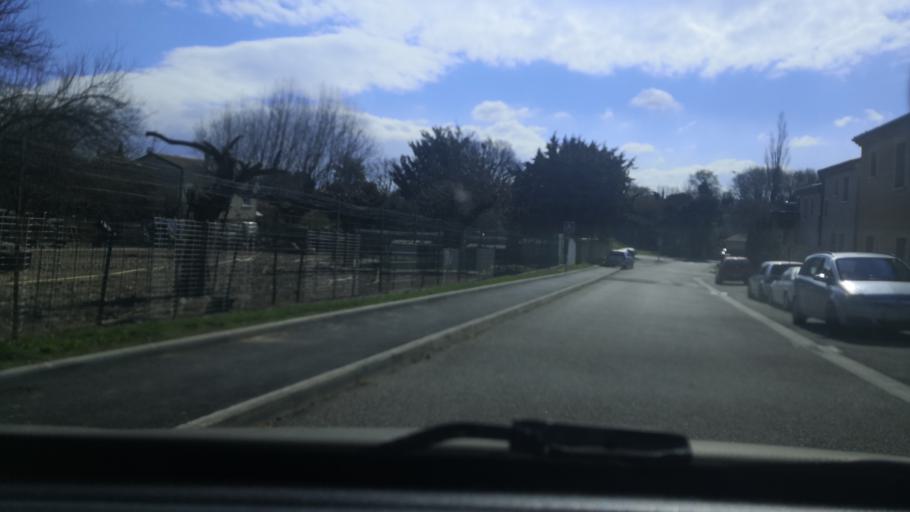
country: FR
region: Rhone-Alpes
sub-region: Departement de la Drome
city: Montboucher-sur-Jabron
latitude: 44.5522
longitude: 4.8035
